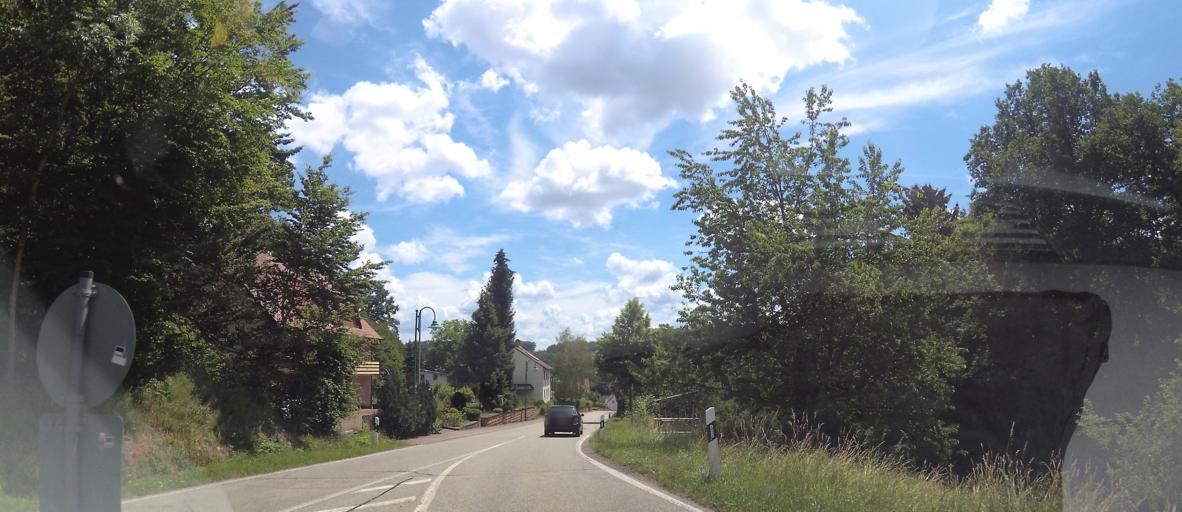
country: DE
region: Rheinland-Pfalz
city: Walshausen
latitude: 49.2138
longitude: 7.4753
